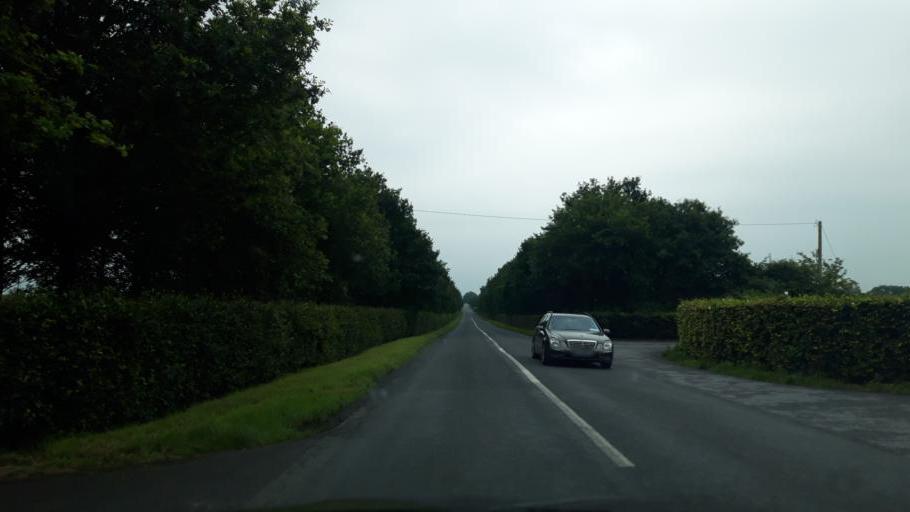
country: IE
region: Munster
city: Fethard
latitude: 52.4984
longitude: -7.6878
